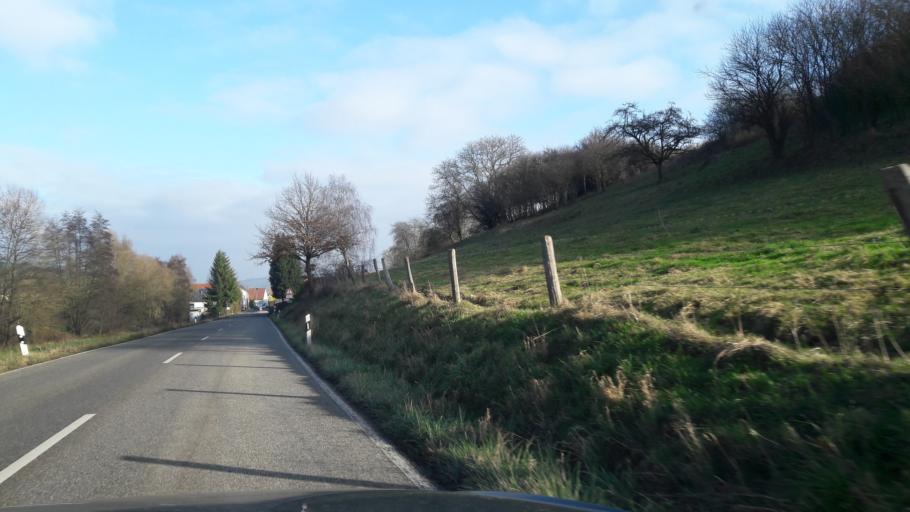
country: DE
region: Rheinland-Pfalz
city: Wahnwegen
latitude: 49.4641
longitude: 7.4040
